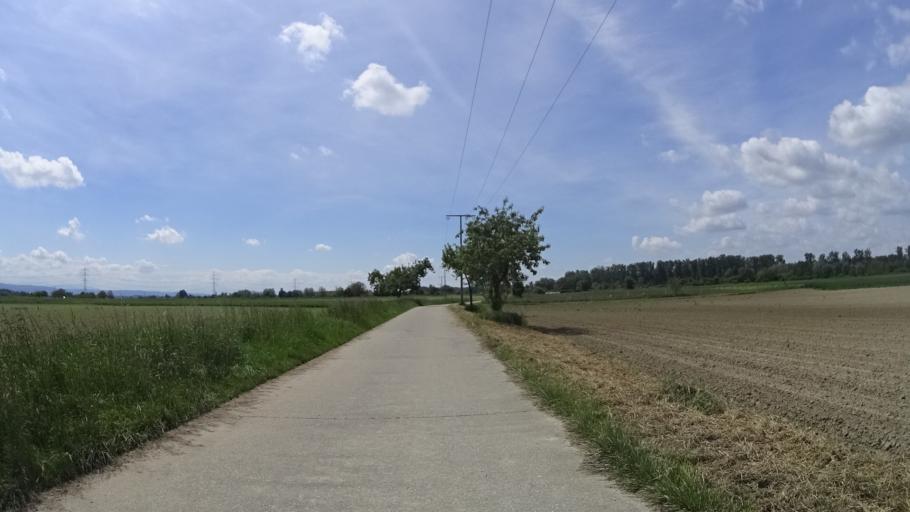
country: DE
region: Baden-Wuerttemberg
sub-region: Freiburg Region
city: Schwanau
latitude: 48.3770
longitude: 7.7533
